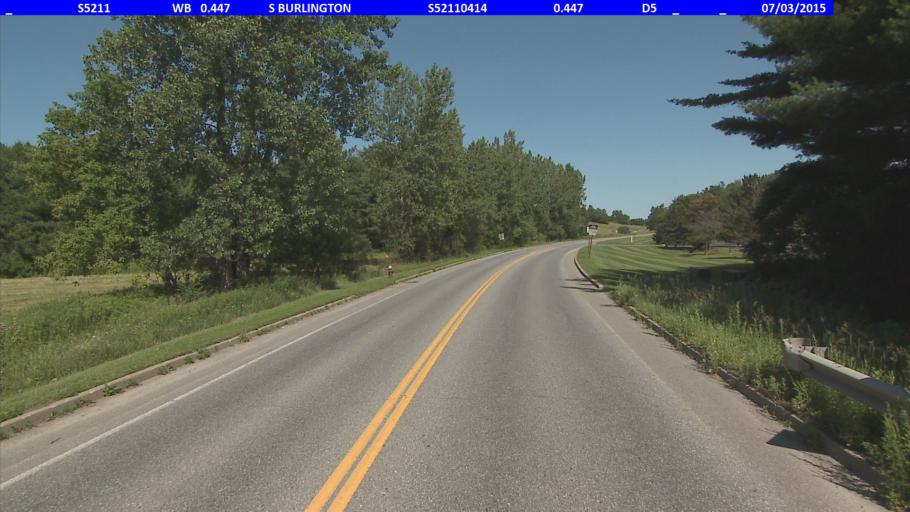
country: US
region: Vermont
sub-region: Chittenden County
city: South Burlington
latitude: 44.4552
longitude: -73.1491
